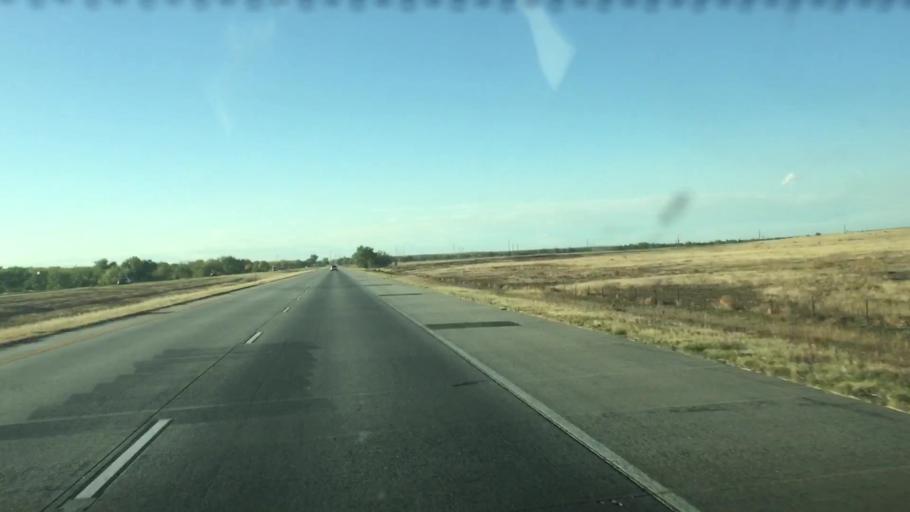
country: US
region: Colorado
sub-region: Arapahoe County
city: Byers
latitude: 39.6414
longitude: -104.0624
